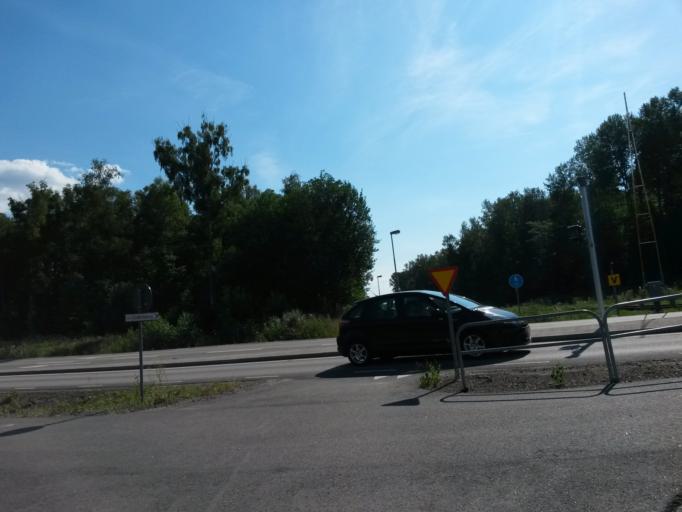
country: SE
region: Vaestra Goetaland
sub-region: Gotene Kommun
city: Kallby
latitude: 58.5037
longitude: 13.2947
